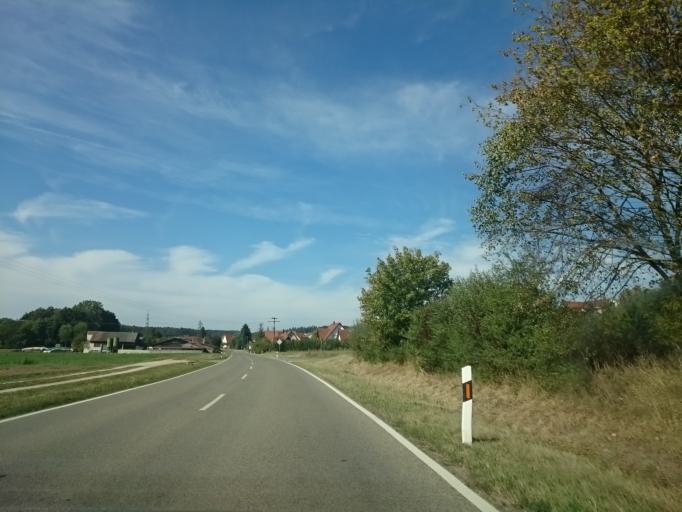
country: DE
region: Bavaria
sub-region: Regierungsbezirk Mittelfranken
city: Heideck
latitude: 49.1325
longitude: 11.0957
